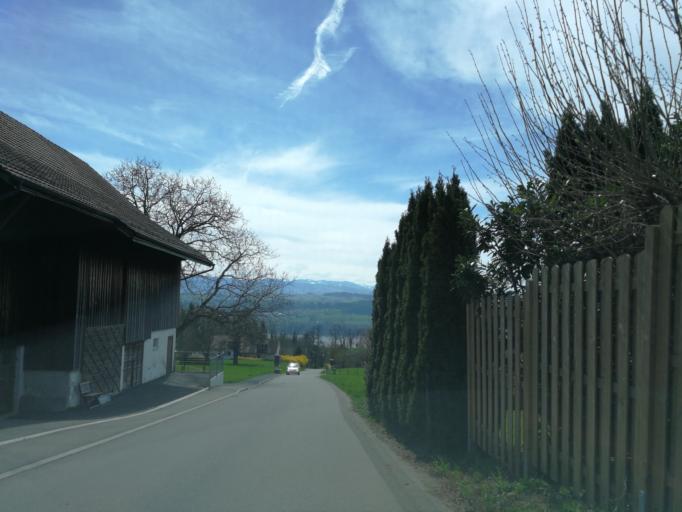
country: CH
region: Zurich
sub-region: Bezirk Meilen
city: Meilen
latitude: 47.2786
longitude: 8.6539
